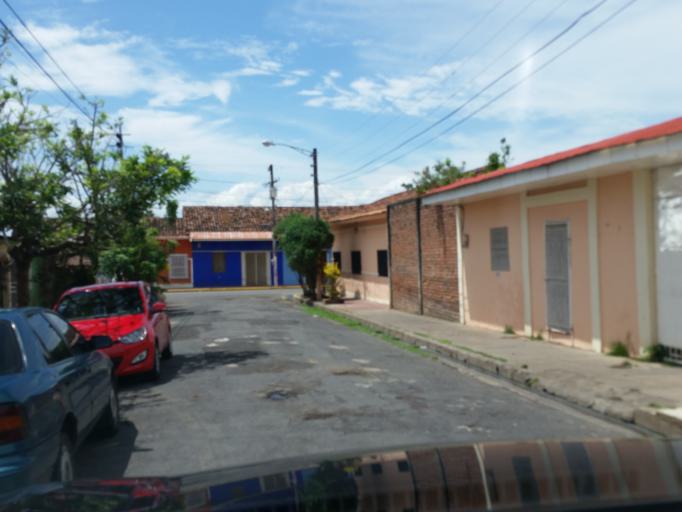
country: NI
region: Granada
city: Granada
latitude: 11.9338
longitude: -85.9503
